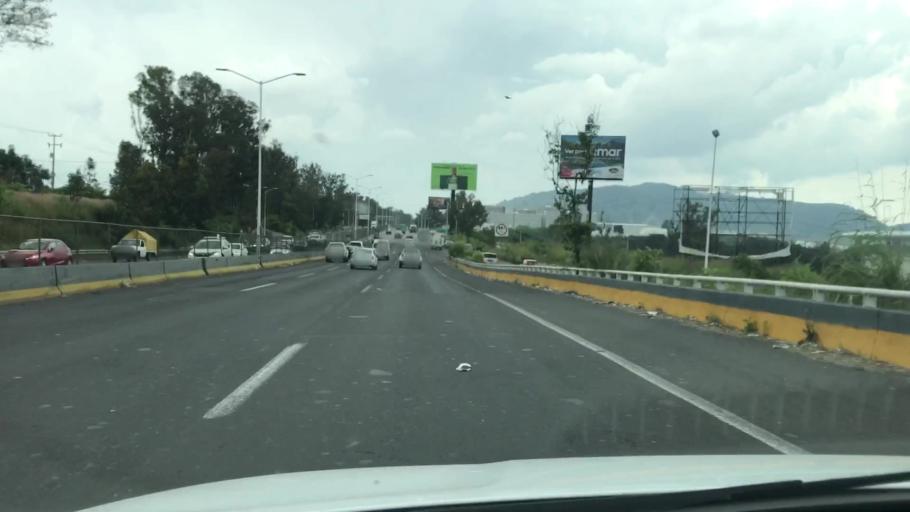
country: MX
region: Jalisco
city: Zapopan2
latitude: 20.6937
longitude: -103.4558
